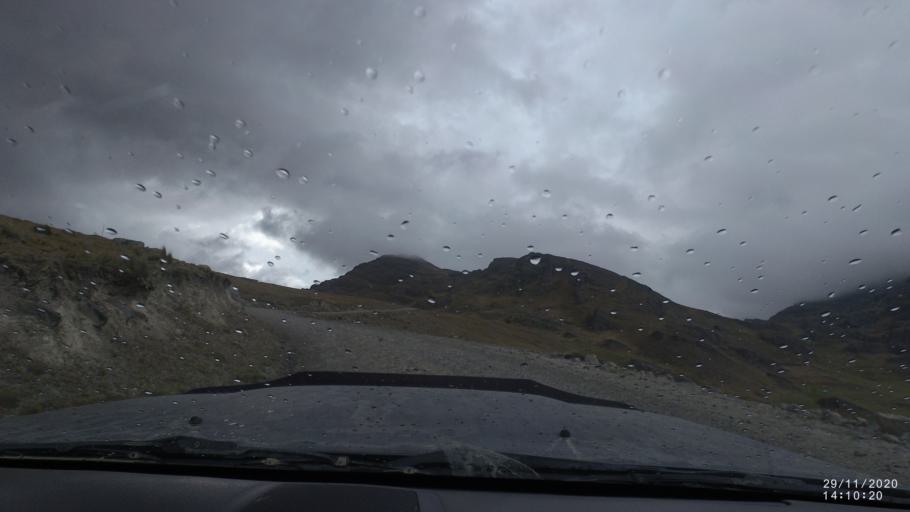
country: BO
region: Cochabamba
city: Sipe Sipe
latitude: -17.2301
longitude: -66.3879
